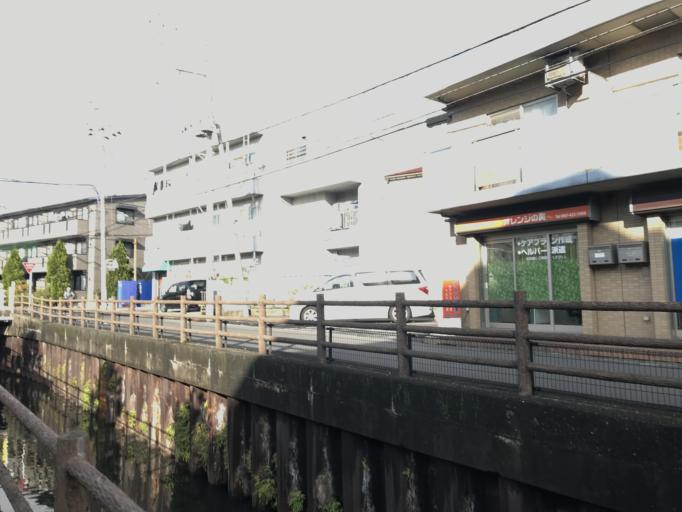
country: JP
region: Chiba
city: Funabashi
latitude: 35.7082
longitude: 139.9845
